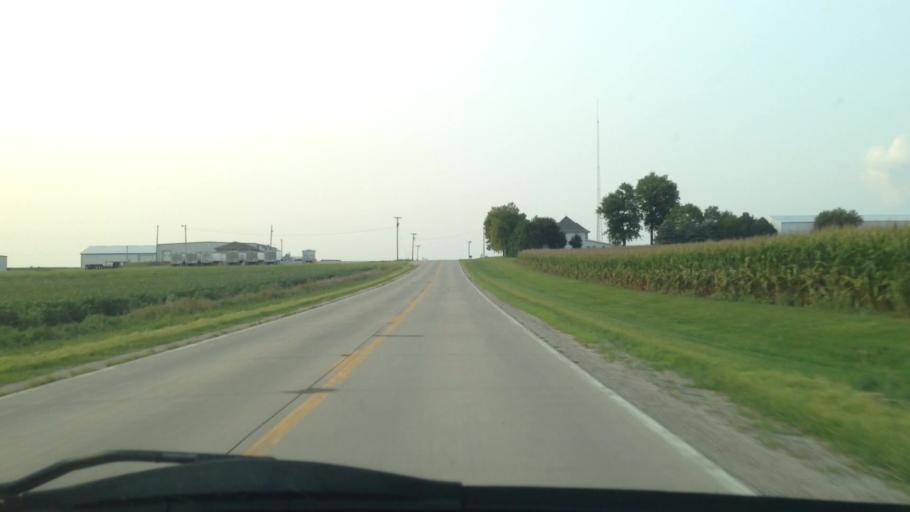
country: US
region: Iowa
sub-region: Benton County
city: Atkins
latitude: 41.9671
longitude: -91.8727
